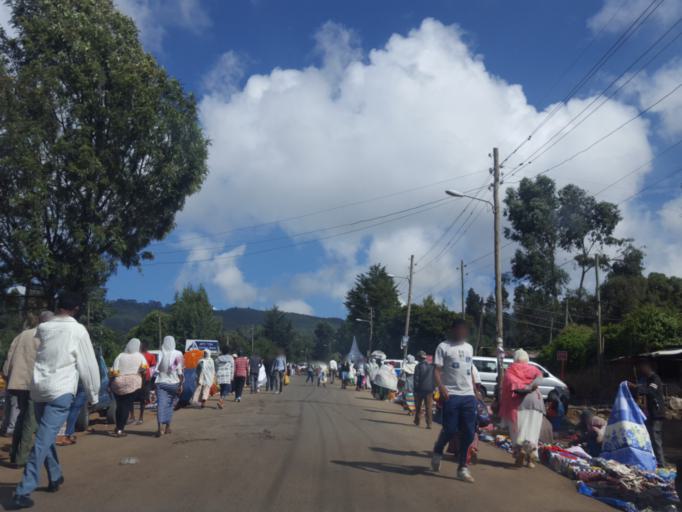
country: ET
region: Adis Abeba
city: Addis Ababa
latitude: 9.0688
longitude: 38.7608
